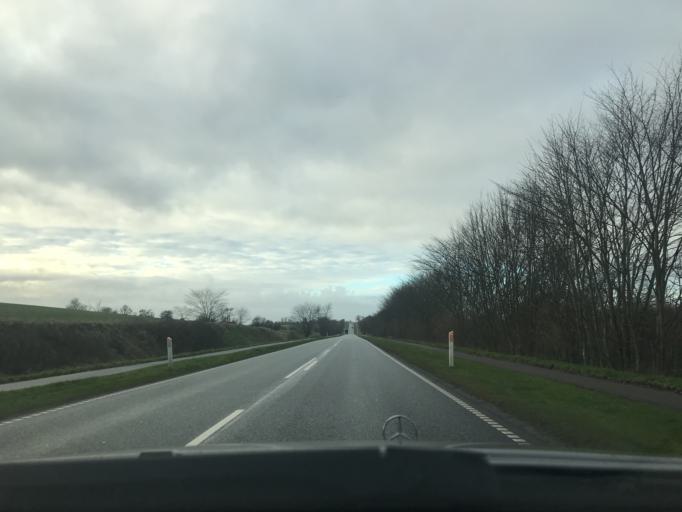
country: DK
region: South Denmark
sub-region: Sonderborg Kommune
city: Dybbol
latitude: 54.9084
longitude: 9.7392
